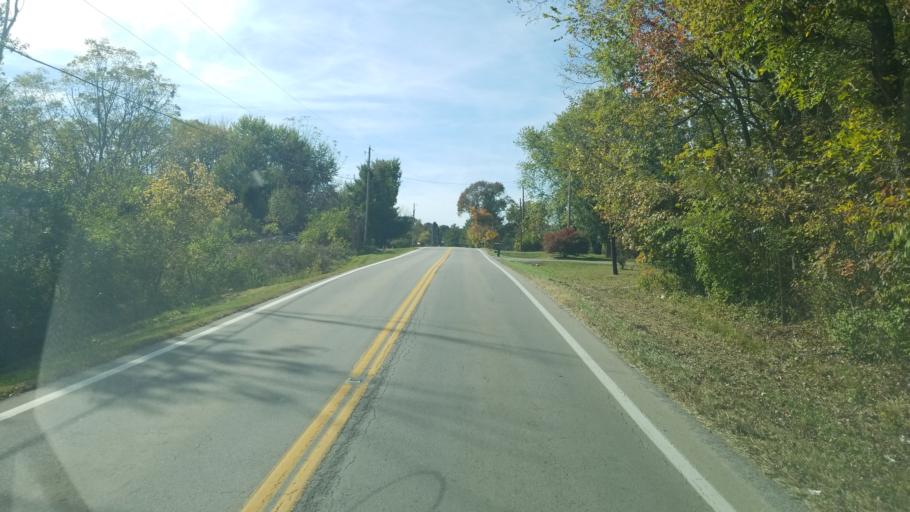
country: US
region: Ohio
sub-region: Clinton County
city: Blanchester
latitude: 39.3799
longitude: -83.9410
